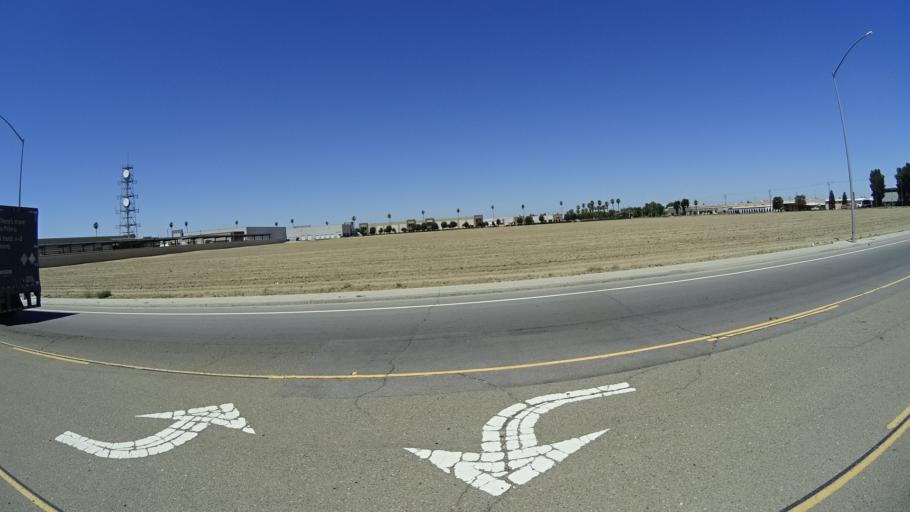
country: US
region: California
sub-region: Fresno County
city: Easton
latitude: 36.6908
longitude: -119.7636
